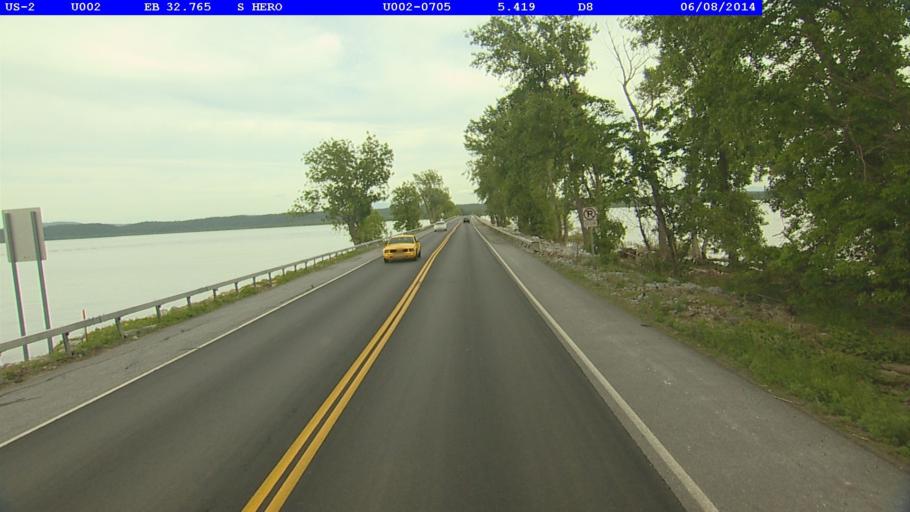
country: US
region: Vermont
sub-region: Chittenden County
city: Colchester
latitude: 44.6337
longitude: -73.2627
